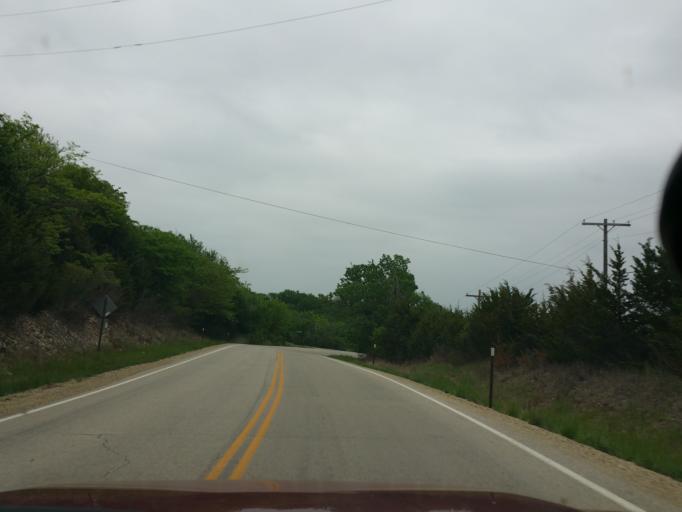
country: US
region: Kansas
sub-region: Riley County
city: Manhattan
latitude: 39.2580
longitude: -96.6160
